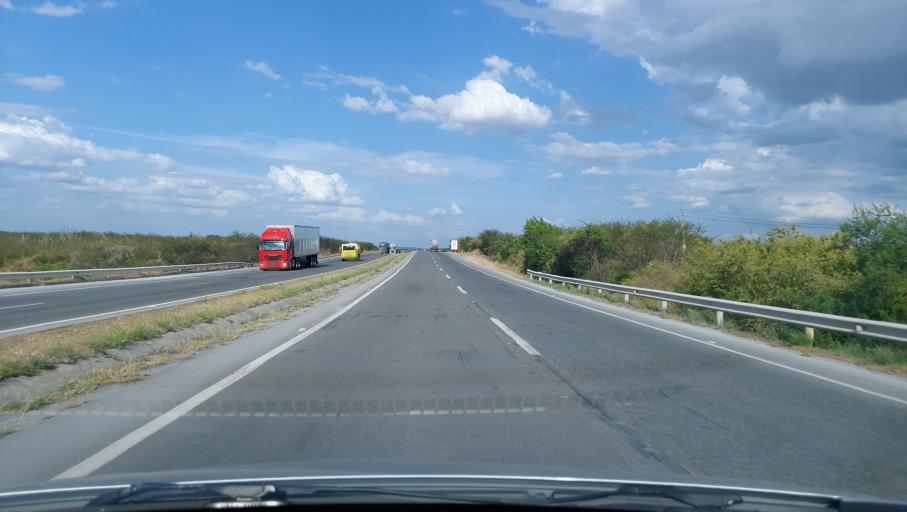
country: BR
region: Bahia
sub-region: Santo Estevao
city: Santo Estevao
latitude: -12.5290
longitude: -39.4090
